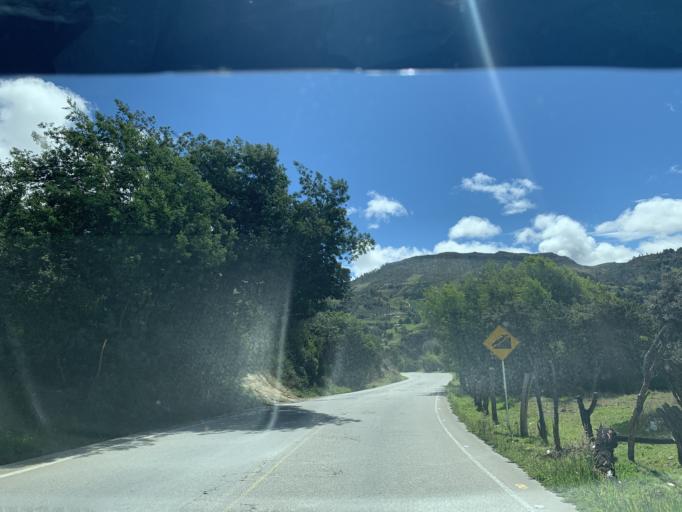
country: CO
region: Boyaca
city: Aquitania
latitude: 5.6122
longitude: -72.8802
